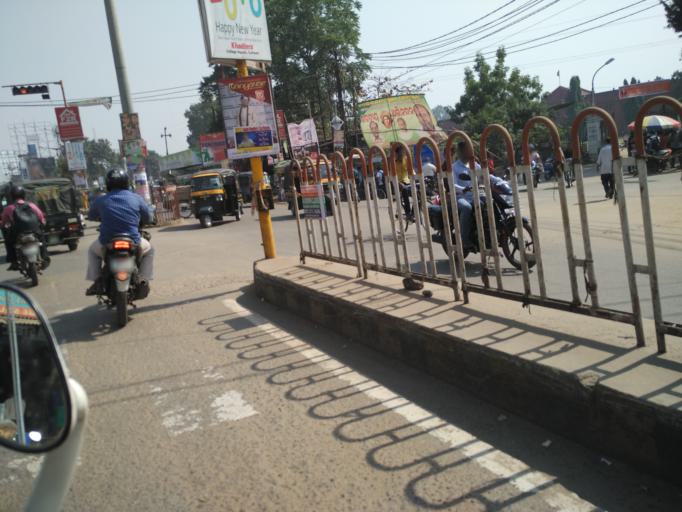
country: IN
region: Odisha
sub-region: Cuttack
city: Cuttack
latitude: 20.4669
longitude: 85.8943
